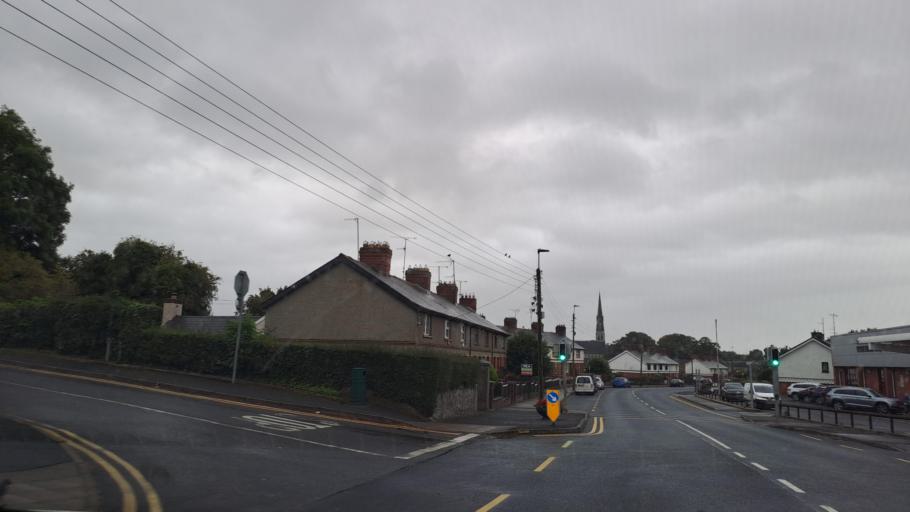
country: IE
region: Ulster
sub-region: County Monaghan
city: Carrickmacross
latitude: 53.9810
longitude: -6.7178
